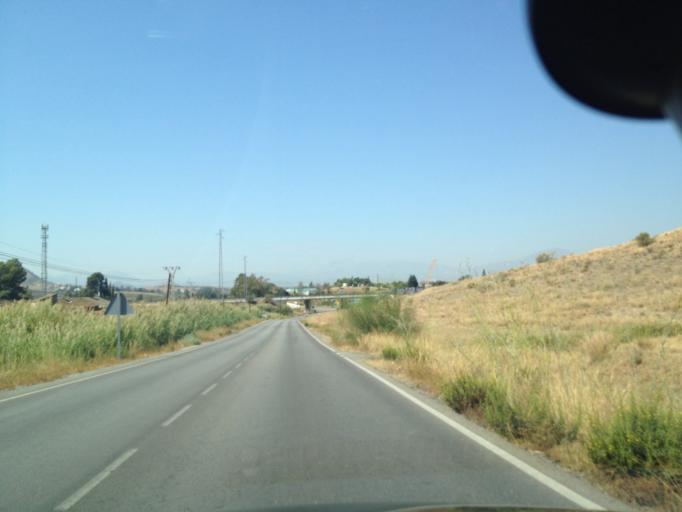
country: ES
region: Andalusia
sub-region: Provincia de Malaga
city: Estacion de Cartama
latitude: 36.7329
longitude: -4.5881
